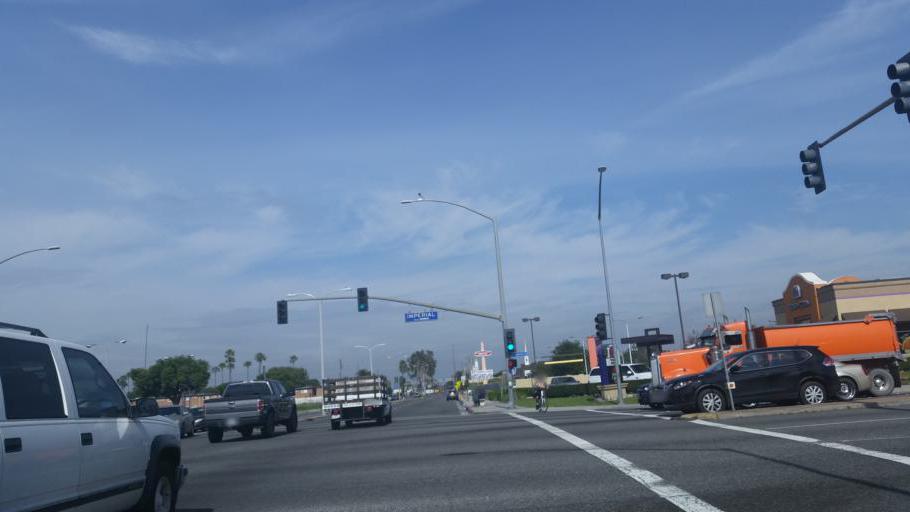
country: US
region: California
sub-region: Los Angeles County
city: Norwalk
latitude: 33.9169
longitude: -118.0991
